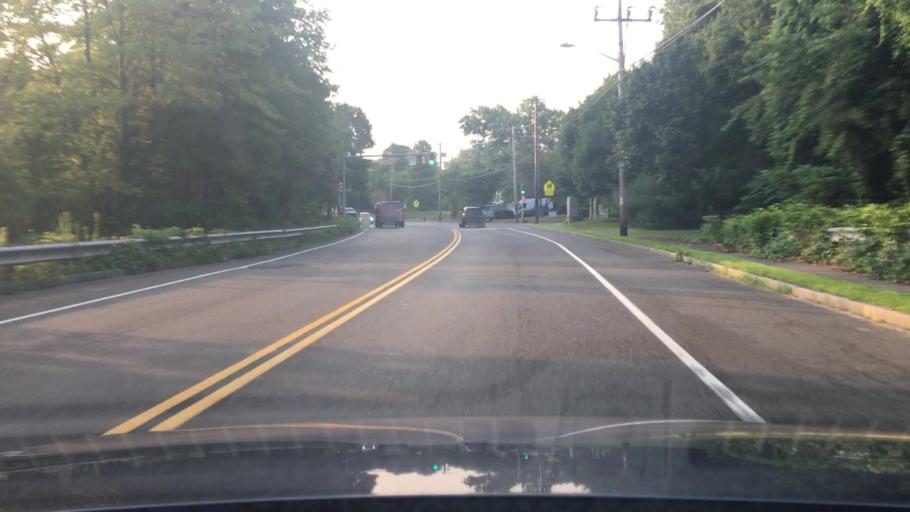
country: US
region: Massachusetts
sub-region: Essex County
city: Saugus
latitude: 42.4776
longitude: -71.0029
